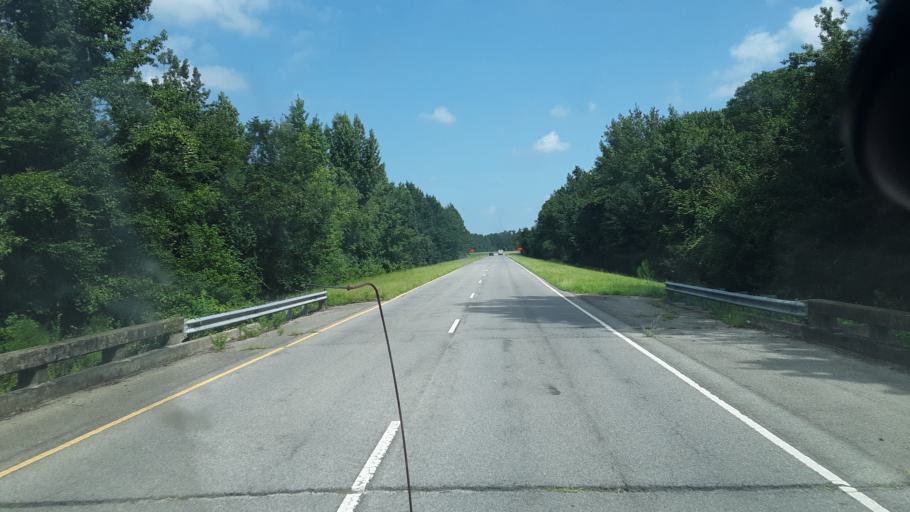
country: US
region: South Carolina
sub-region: Bamberg County
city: Bamberg
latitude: 33.3411
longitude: -81.0175
